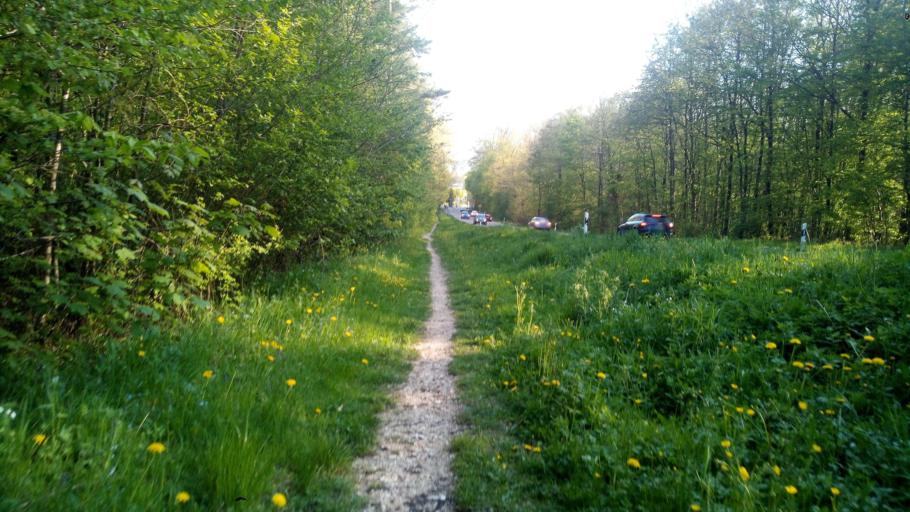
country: DE
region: Baden-Wuerttemberg
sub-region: Regierungsbezirk Stuttgart
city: Goeppingen
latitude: 48.7164
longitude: 9.6777
